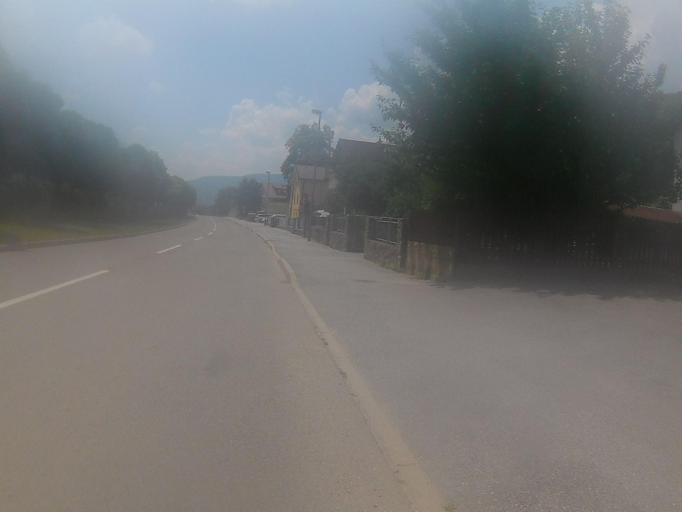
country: SI
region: Maribor
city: Kamnica
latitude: 46.5786
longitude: 15.6134
